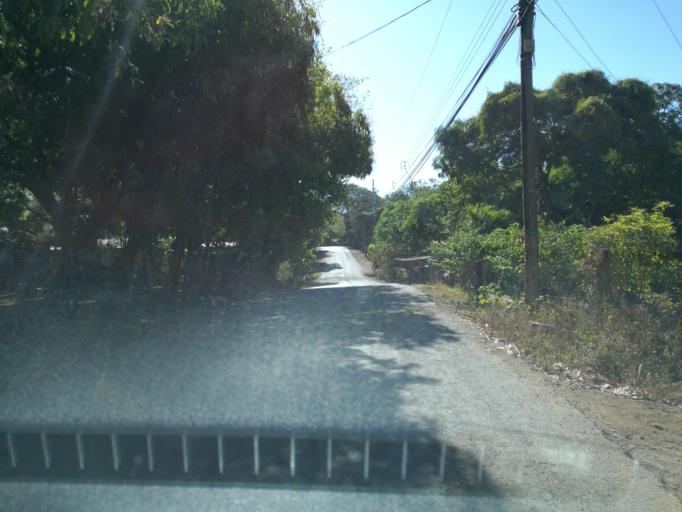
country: CR
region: Guanacaste
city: Juntas
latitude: 10.0964
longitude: -84.9835
